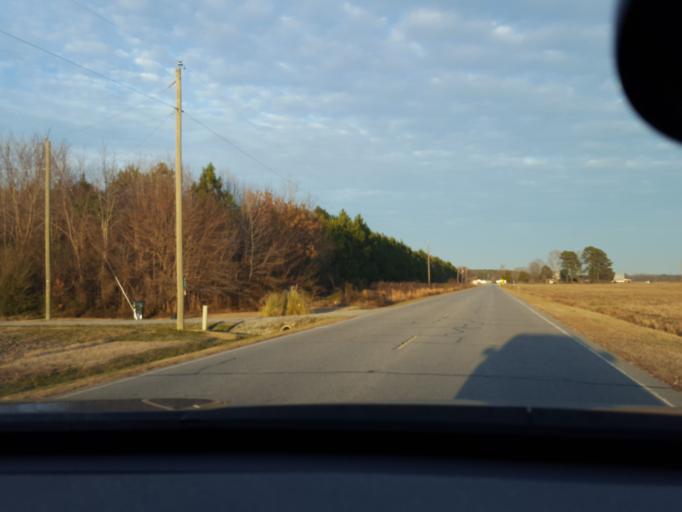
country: US
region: North Carolina
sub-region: Hertford County
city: Murfreesboro
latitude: 36.2842
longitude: -77.1944
